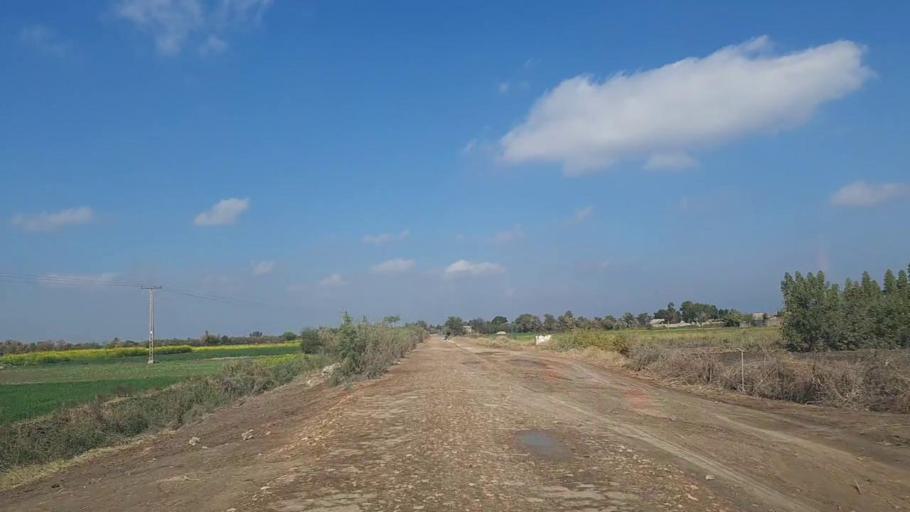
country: PK
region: Sindh
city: Sanghar
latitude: 26.0758
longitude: 68.9865
